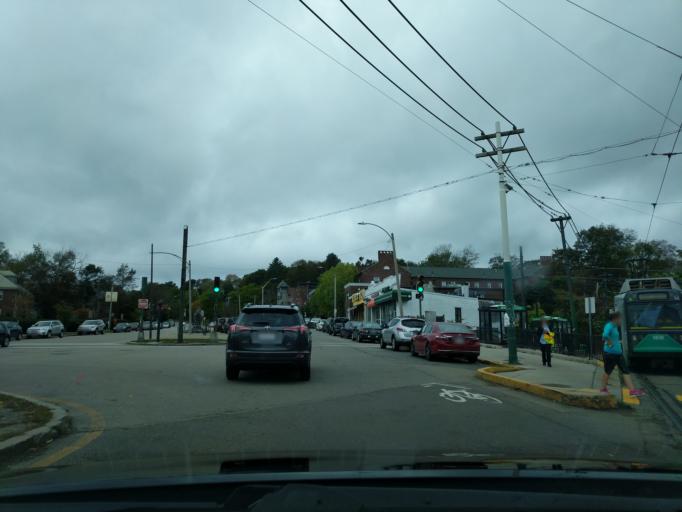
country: US
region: Massachusetts
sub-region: Middlesex County
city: Watertown
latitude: 42.3400
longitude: -71.1666
